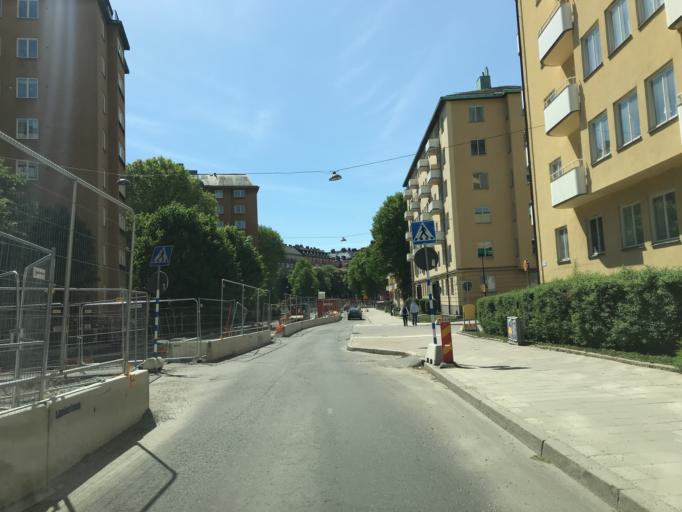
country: SE
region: Stockholm
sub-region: Stockholms Kommun
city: OEstermalm
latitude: 59.3412
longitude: 18.0963
